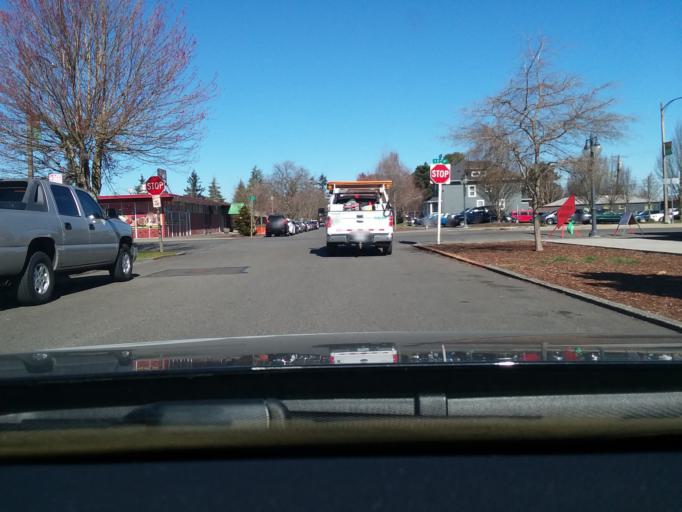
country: US
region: Washington
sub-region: Pierce County
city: Tacoma
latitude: 47.2516
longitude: -122.4530
